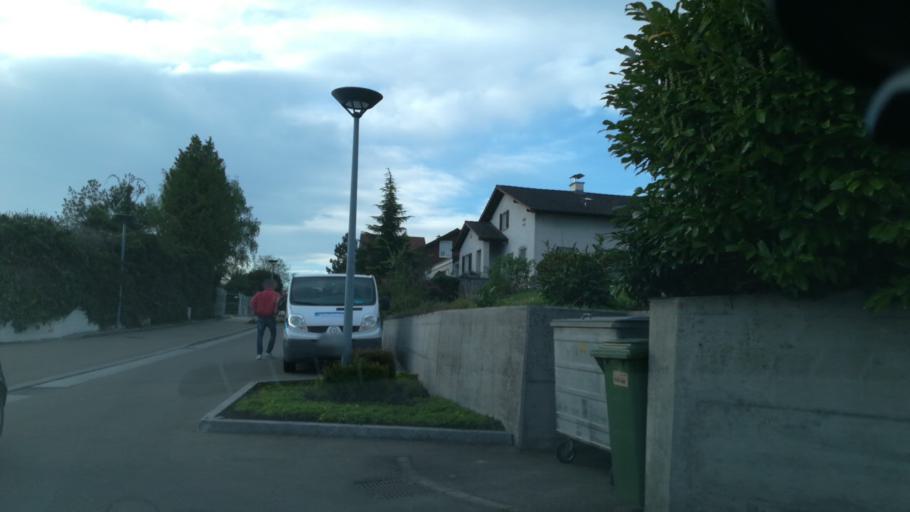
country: CH
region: Zurich
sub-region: Bezirk Uster
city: Gockhausen
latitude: 47.3811
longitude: 8.6003
